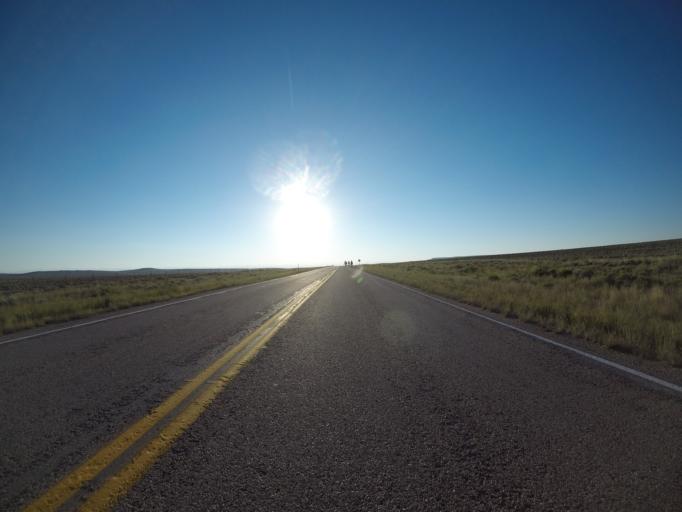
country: US
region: Wyoming
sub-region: Sublette County
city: Marbleton
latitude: 42.5791
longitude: -110.0044
